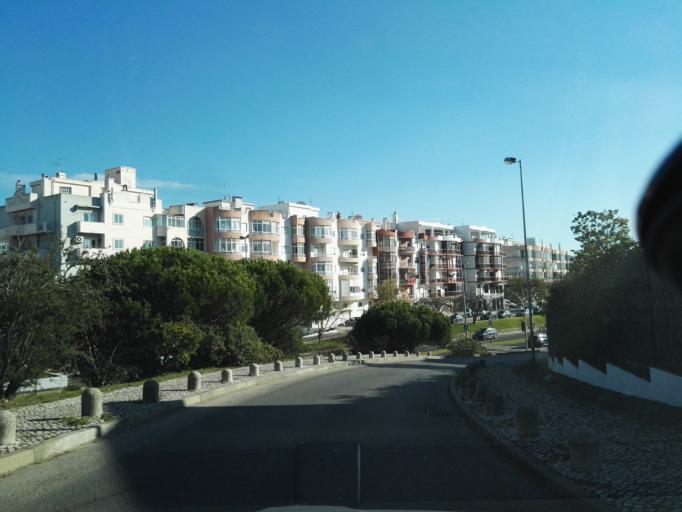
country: PT
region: Setubal
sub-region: Almada
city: Pragal
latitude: 38.6550
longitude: -9.1668
